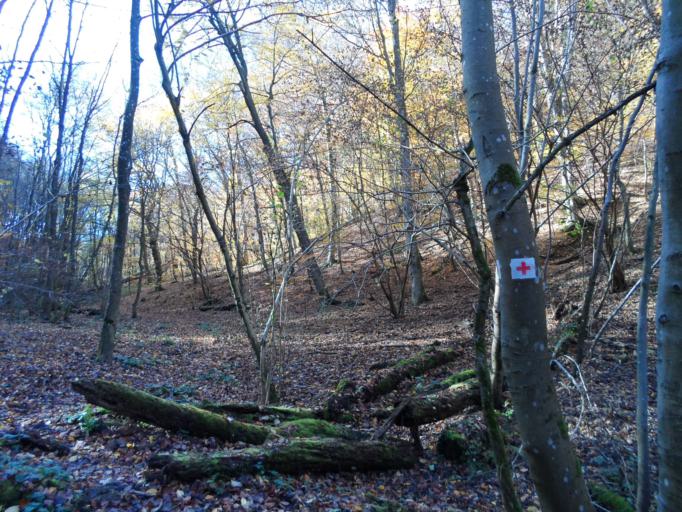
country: HU
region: Veszprem
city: Varpalota
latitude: 47.2581
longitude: 18.1127
